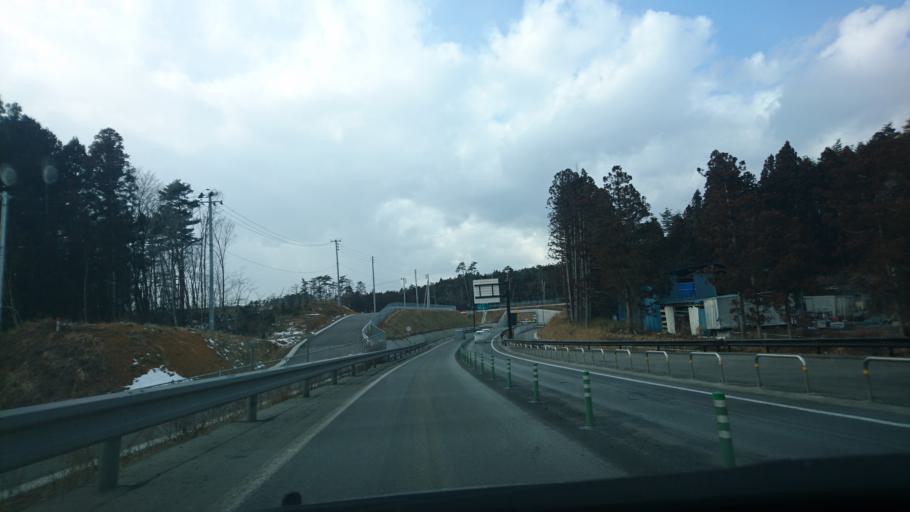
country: JP
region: Miyagi
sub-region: Oshika Gun
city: Onagawa Cho
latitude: 38.6917
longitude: 141.4645
